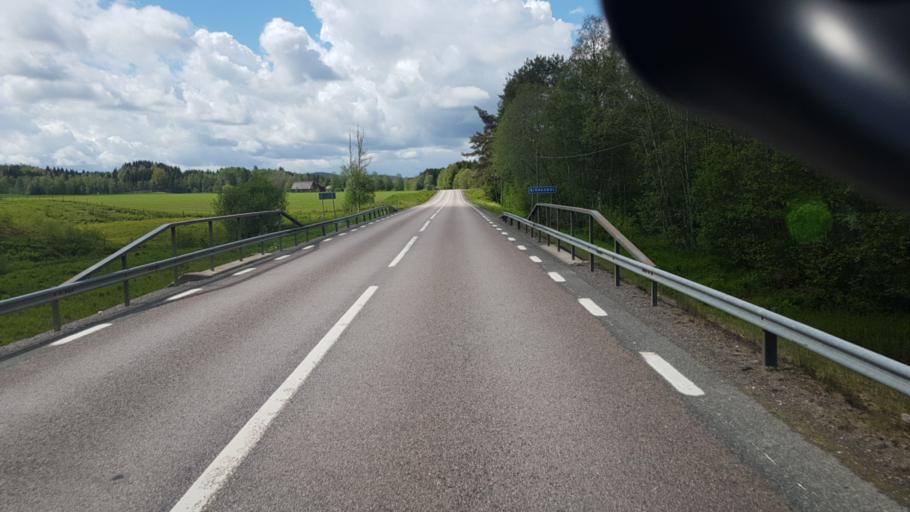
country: SE
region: Vaermland
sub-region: Arjangs Kommun
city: Arjaeng
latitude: 59.5999
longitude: 12.1498
